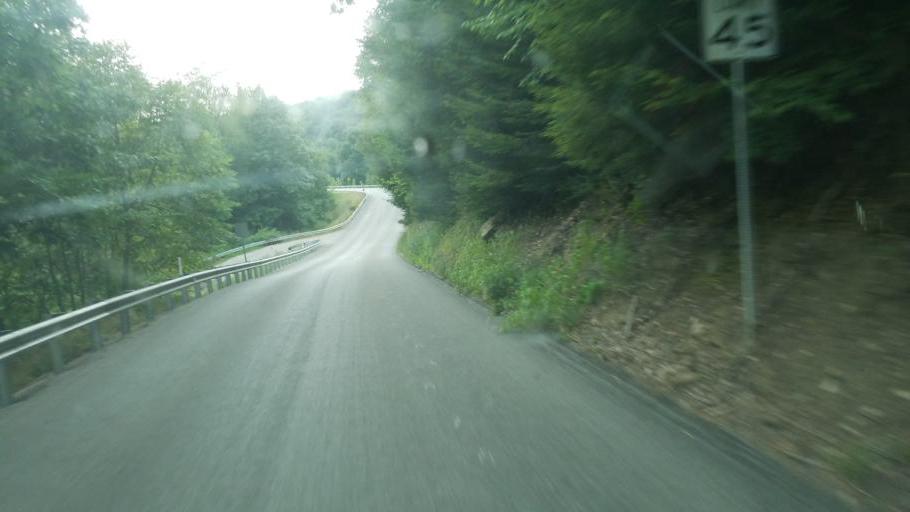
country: US
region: Pennsylvania
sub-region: Clarion County
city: Knox
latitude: 41.1633
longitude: -79.5344
